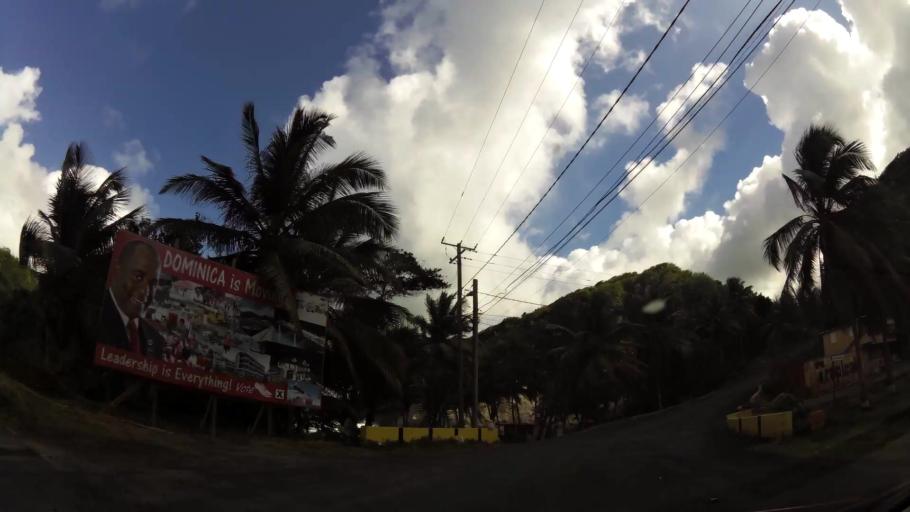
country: DM
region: Saint Andrew
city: Calibishie
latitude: 15.6000
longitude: -61.3949
